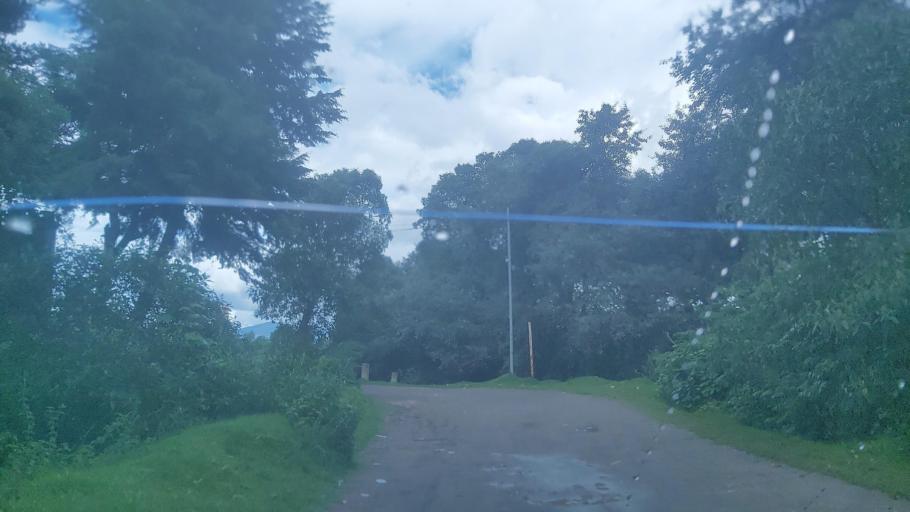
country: GT
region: Quetzaltenango
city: Quetzaltenango
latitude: 14.8530
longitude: -91.5397
